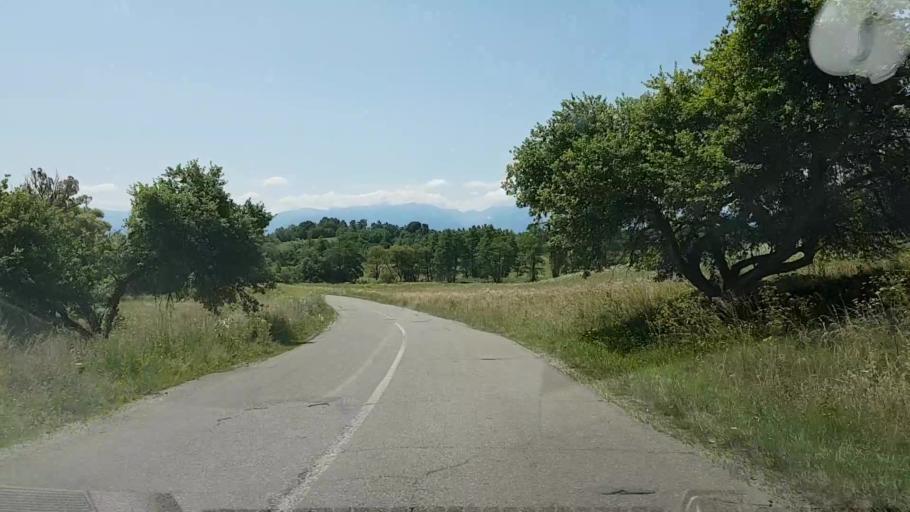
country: RO
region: Brasov
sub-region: Comuna Voila
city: Voila
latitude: 45.8629
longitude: 24.8254
